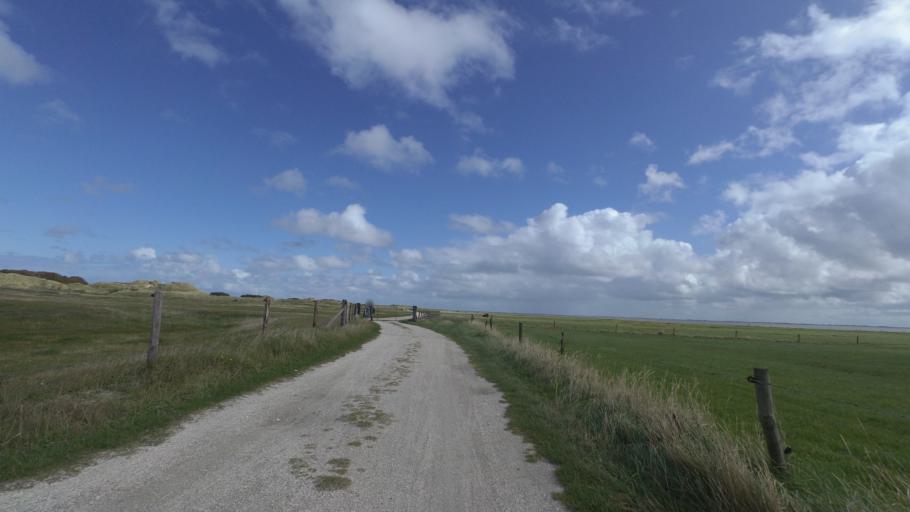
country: NL
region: Friesland
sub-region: Gemeente Ameland
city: Nes
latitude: 53.4473
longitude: 5.8522
